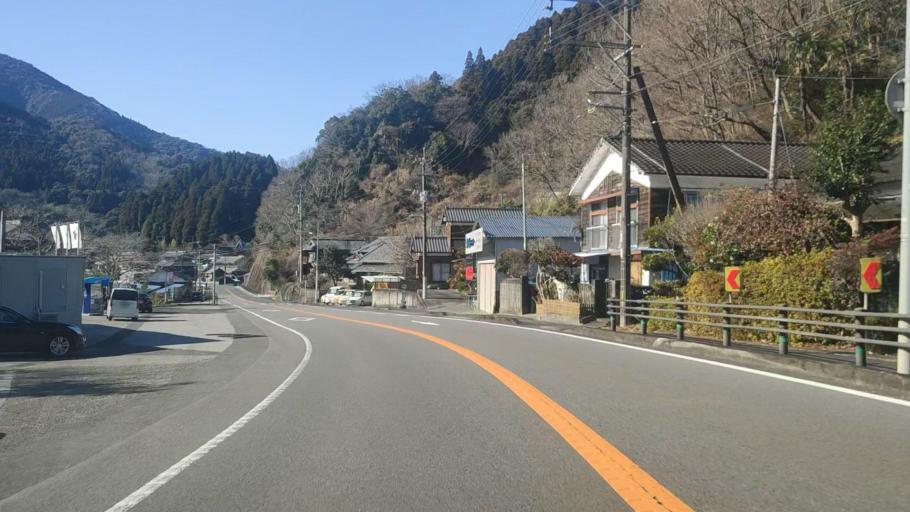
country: JP
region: Oita
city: Saiki
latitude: 32.9950
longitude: 131.8275
